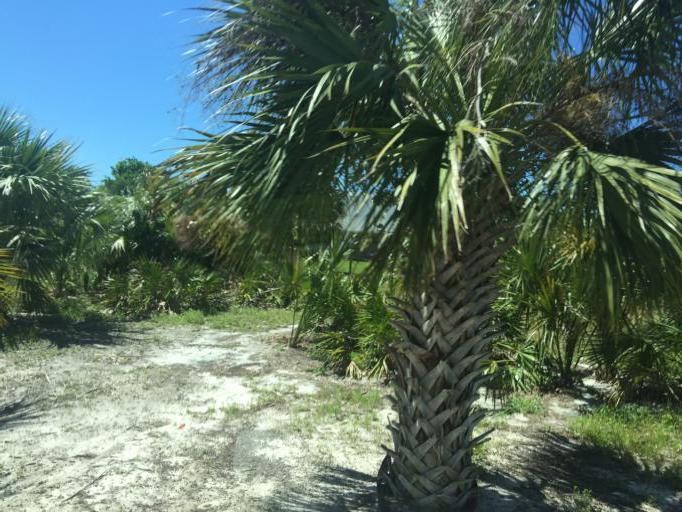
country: US
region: Florida
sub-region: Bay County
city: Panama City Beach
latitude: 30.2004
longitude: -85.8437
